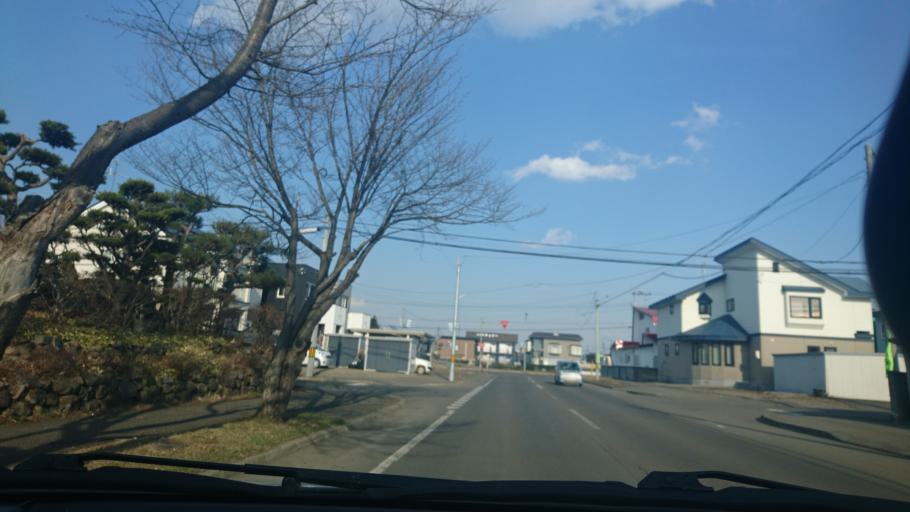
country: JP
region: Hokkaido
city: Obihiro
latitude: 42.9212
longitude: 143.1567
